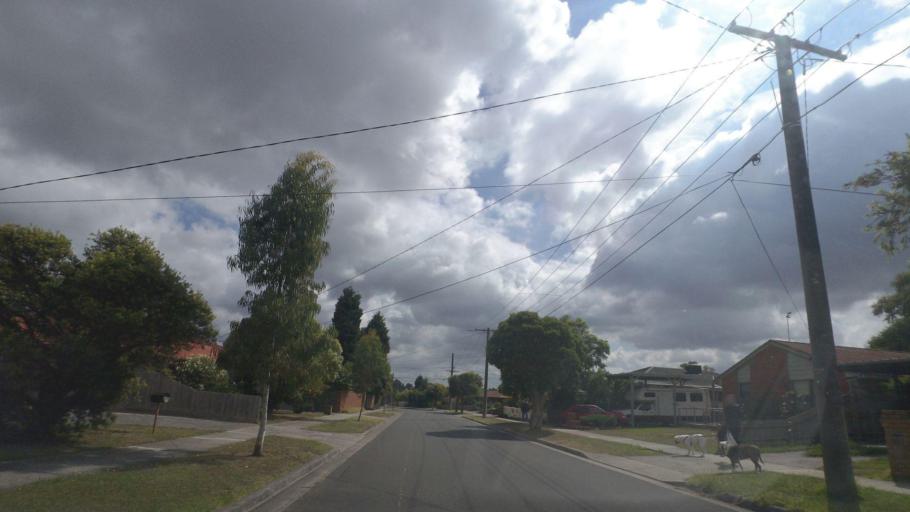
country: AU
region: Victoria
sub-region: Knox
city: Scoresby
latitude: -37.8979
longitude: 145.2290
